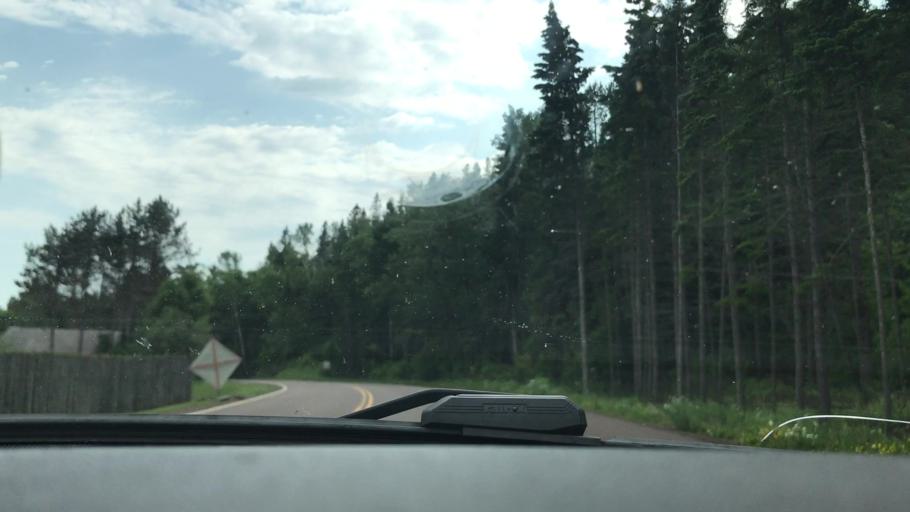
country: CA
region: Ontario
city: Neebing
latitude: 47.9630
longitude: -89.6854
